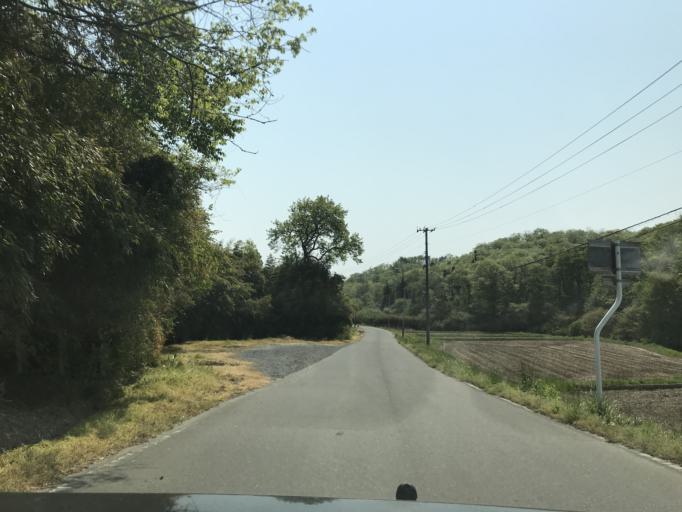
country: JP
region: Iwate
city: Ichinoseki
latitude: 38.8484
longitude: 141.0568
